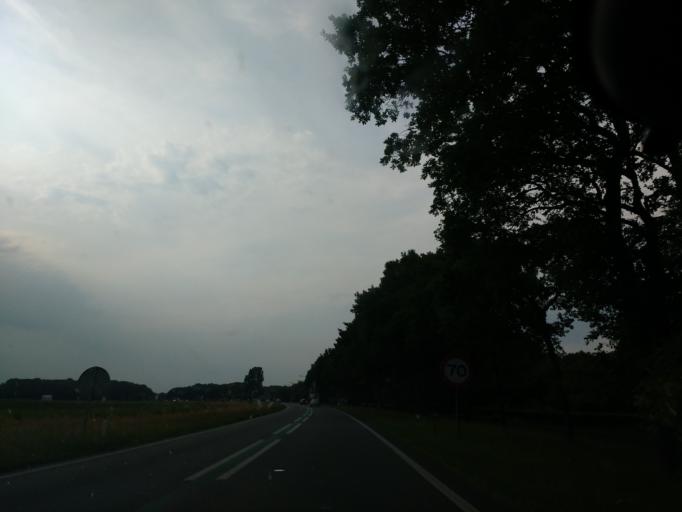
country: NL
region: Drenthe
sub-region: Gemeente Borger-Odoorn
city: Borger
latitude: 52.8979
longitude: 6.8150
